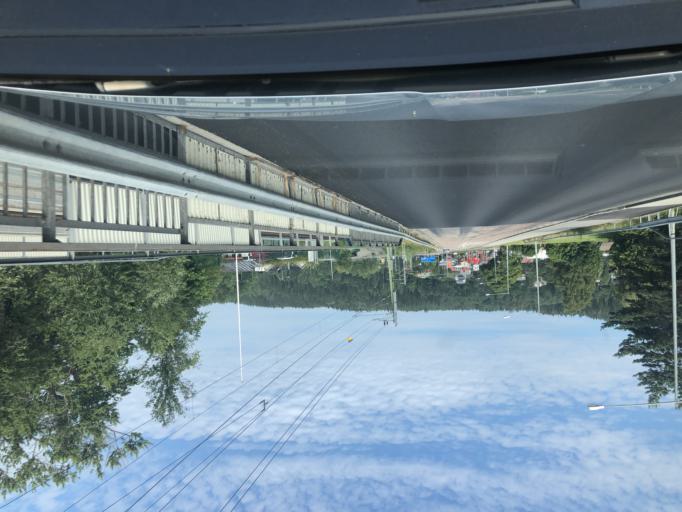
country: SE
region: Vaesternorrland
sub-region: Kramfors Kommun
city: Kramfors
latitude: 62.9324
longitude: 17.7739
